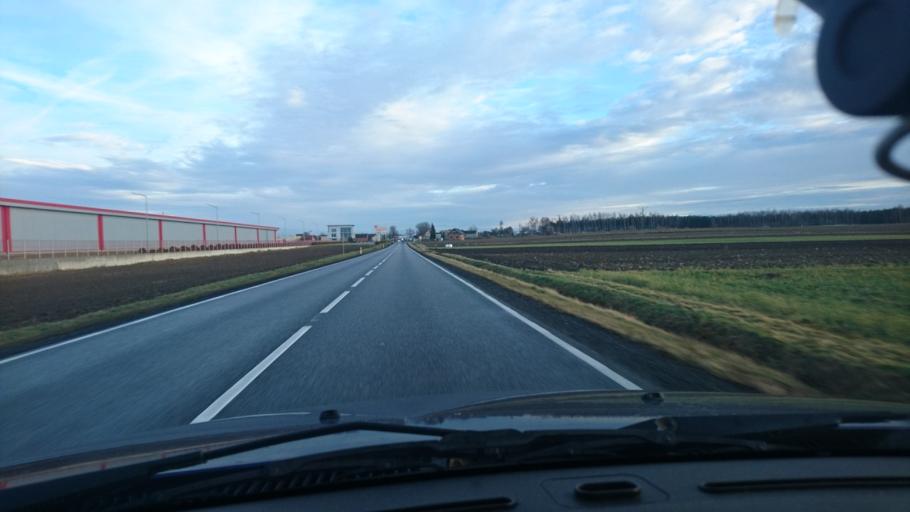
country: PL
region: Greater Poland Voivodeship
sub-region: Powiat kepinski
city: Slupia pod Kepnem
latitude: 51.2320
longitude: 18.0682
